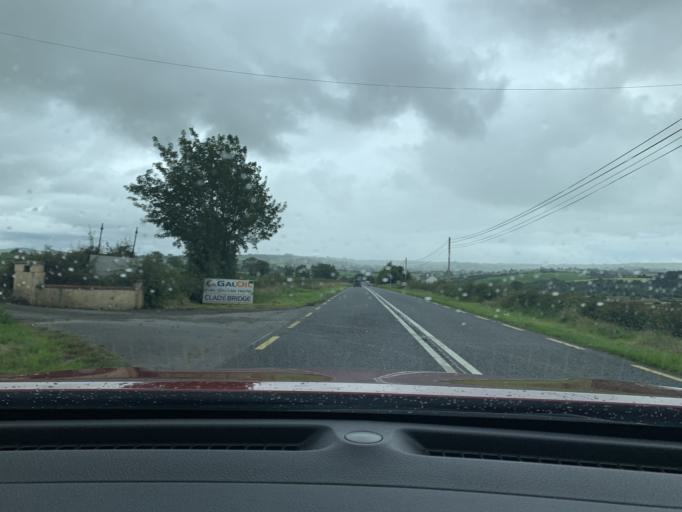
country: IE
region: Ulster
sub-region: County Donegal
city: Leifear
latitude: 54.7958
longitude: -7.5615
